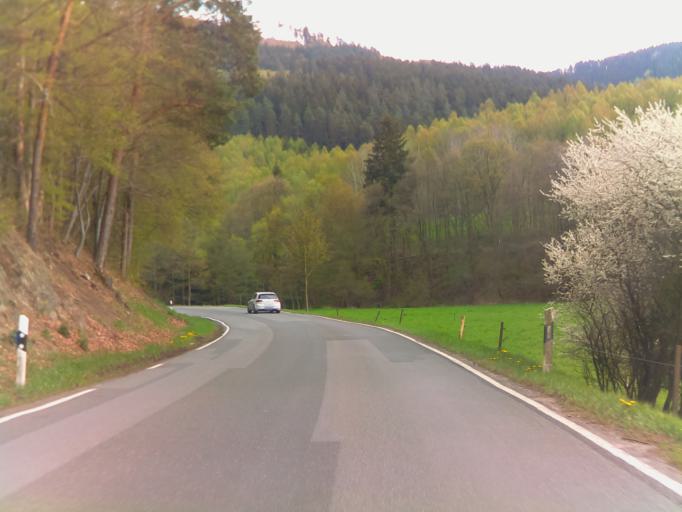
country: DE
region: Thuringia
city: Grafenthal
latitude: 50.5277
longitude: 11.3356
